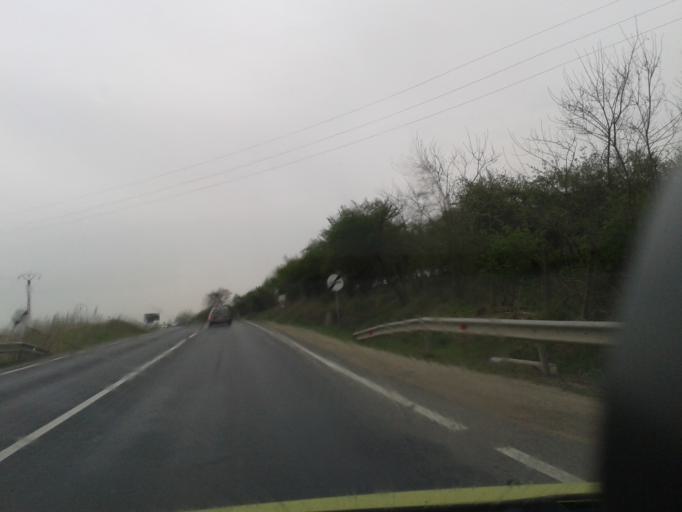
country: RO
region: Hunedoara
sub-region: Oras Simeria
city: Simeria
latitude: 45.8497
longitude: 22.9808
